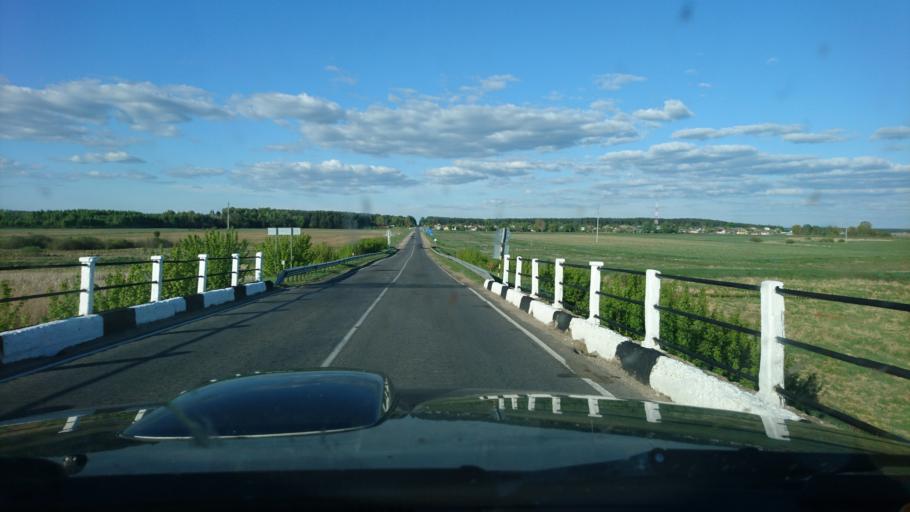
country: BY
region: Brest
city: Ivatsevichy
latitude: 52.7203
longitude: 25.3602
